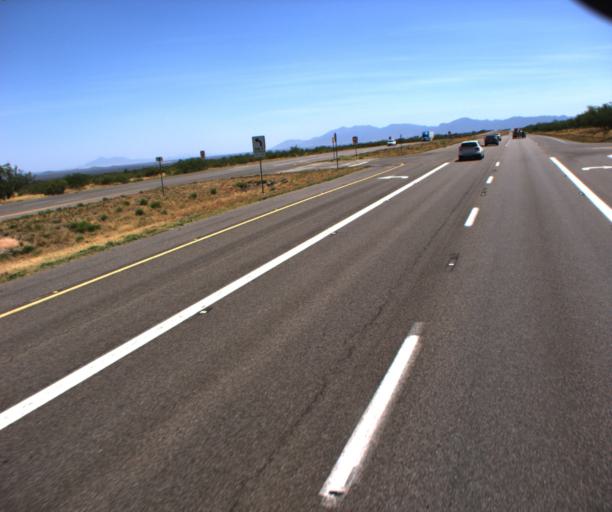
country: US
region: Arizona
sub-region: Cochise County
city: Whetstone
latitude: 31.8362
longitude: -110.3436
